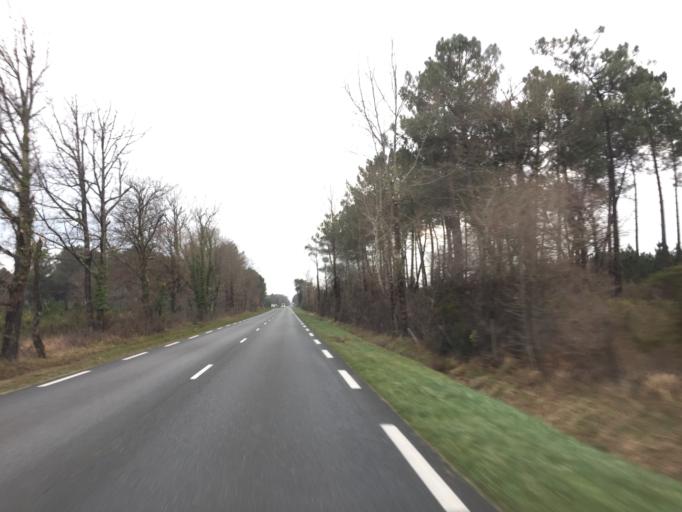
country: FR
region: Aquitaine
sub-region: Departement de la Gironde
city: Saint-Sauveur
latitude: 45.1796
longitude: -0.8427
